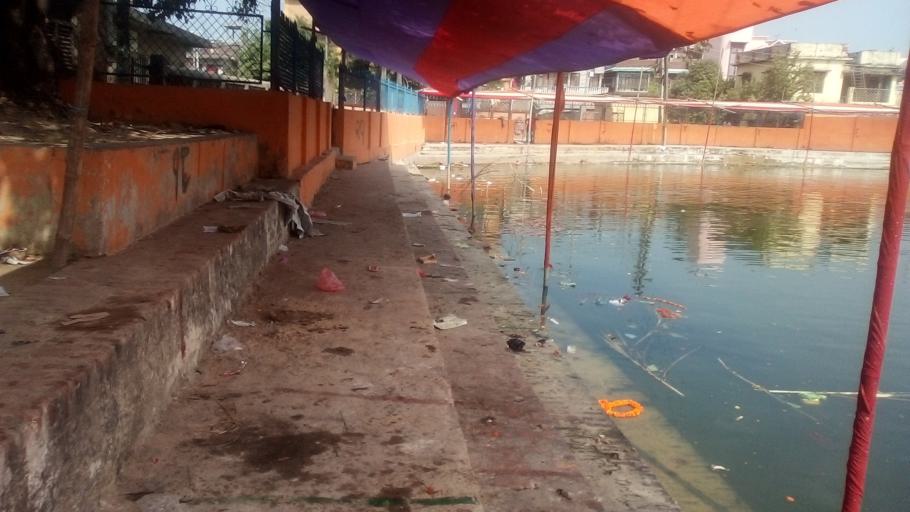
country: NP
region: Central Region
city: Janakpur
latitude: 26.7324
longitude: 85.9247
